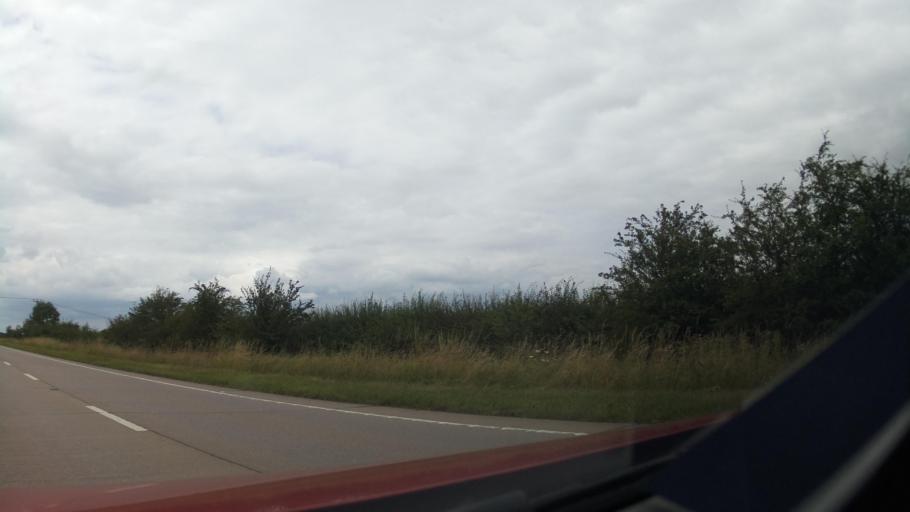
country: GB
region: England
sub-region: Lincolnshire
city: Long Bennington
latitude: 52.9353
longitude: -0.8198
